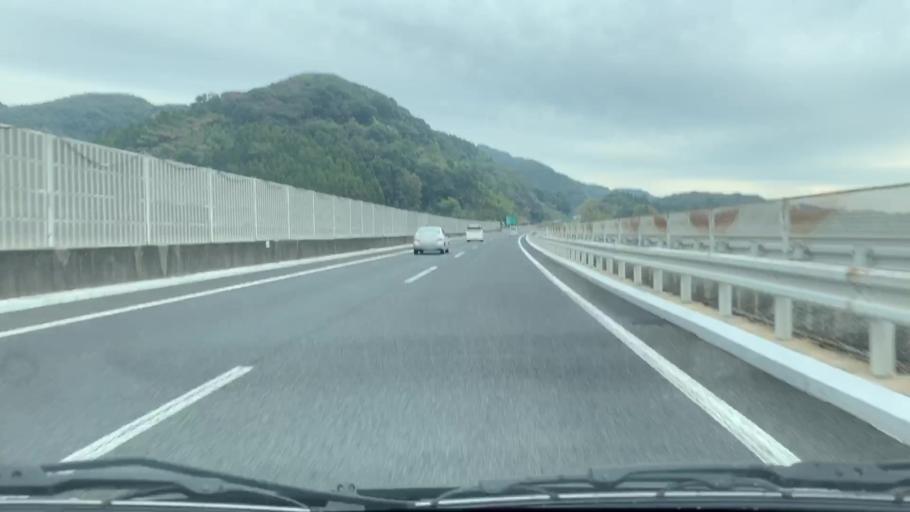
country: JP
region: Saga Prefecture
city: Saga-shi
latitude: 33.2964
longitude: 130.1734
